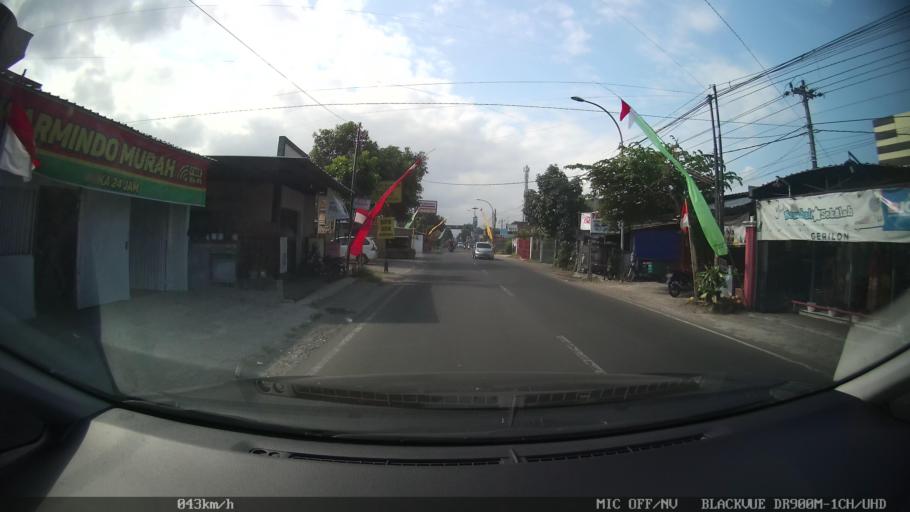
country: ID
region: Daerah Istimewa Yogyakarta
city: Sewon
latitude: -7.8556
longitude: 110.3900
